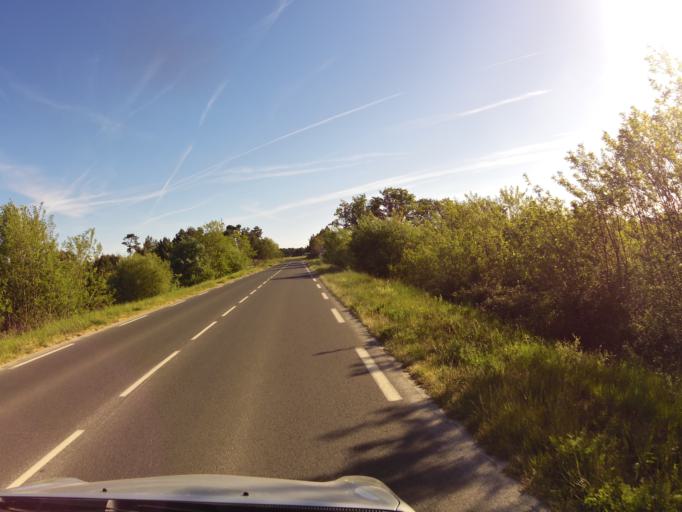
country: FR
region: Aquitaine
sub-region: Departement de la Dordogne
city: Sarlat-la-Caneda
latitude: 44.9535
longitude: 1.2249
